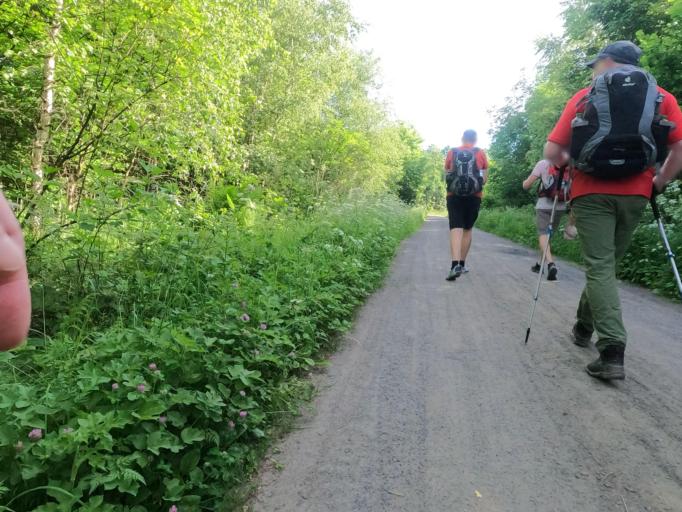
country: DE
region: Rheinland-Pfalz
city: Bad Marienberg
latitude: 50.6613
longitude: 7.9441
